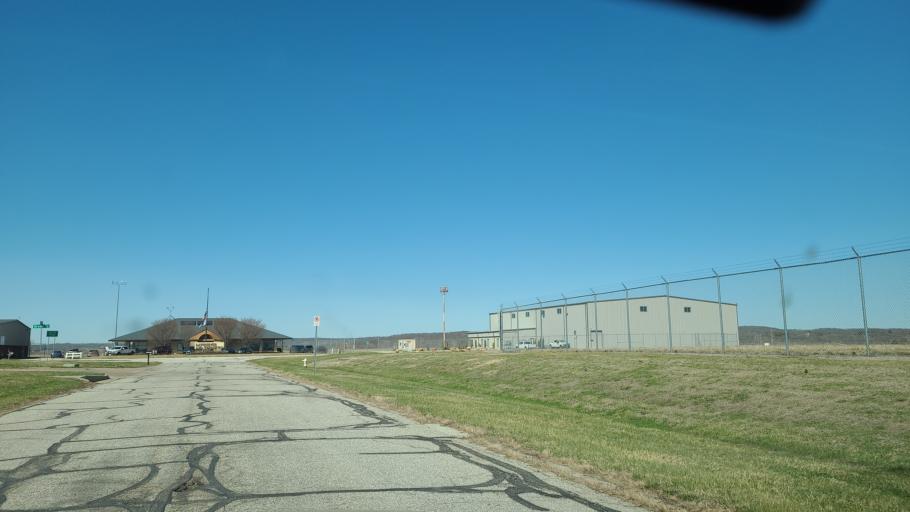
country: US
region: Kansas
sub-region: Douglas County
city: Lawrence
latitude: 39.0038
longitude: -95.2161
